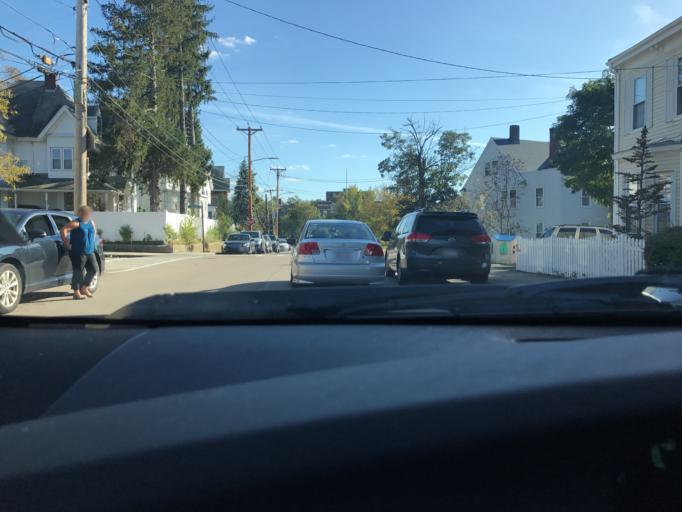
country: US
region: Massachusetts
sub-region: Suffolk County
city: Jamaica Plain
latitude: 42.2650
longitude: -71.1180
